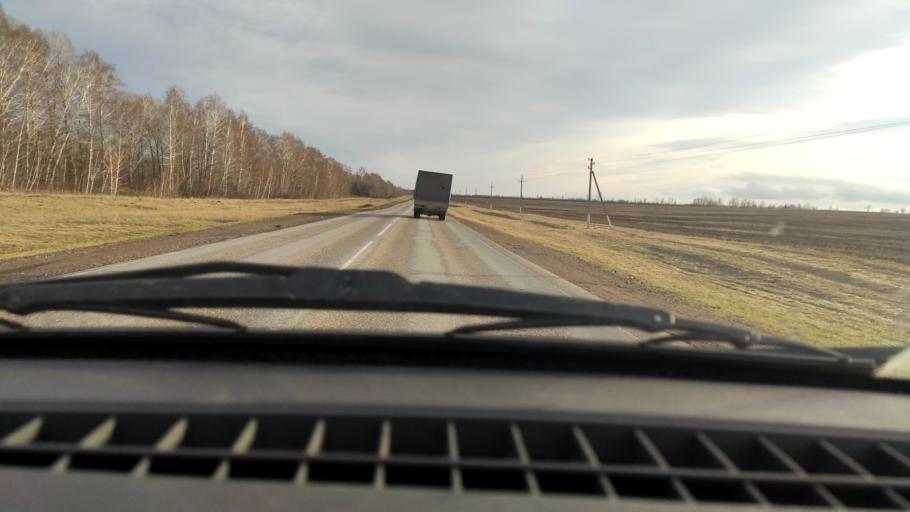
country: RU
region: Bashkortostan
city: Davlekanovo
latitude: 54.3407
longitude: 55.1724
